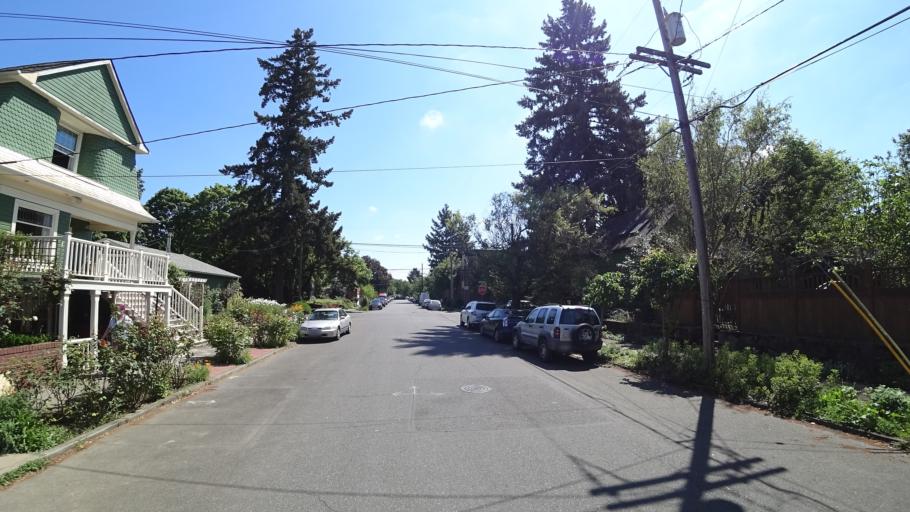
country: US
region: Oregon
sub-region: Multnomah County
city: Portland
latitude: 45.5088
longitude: -122.6282
